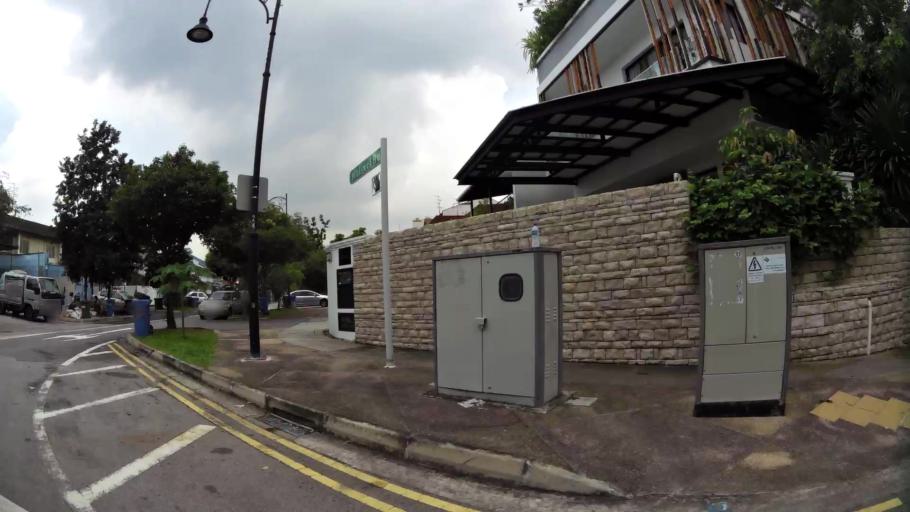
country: SG
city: Singapore
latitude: 1.3462
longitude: 103.8667
